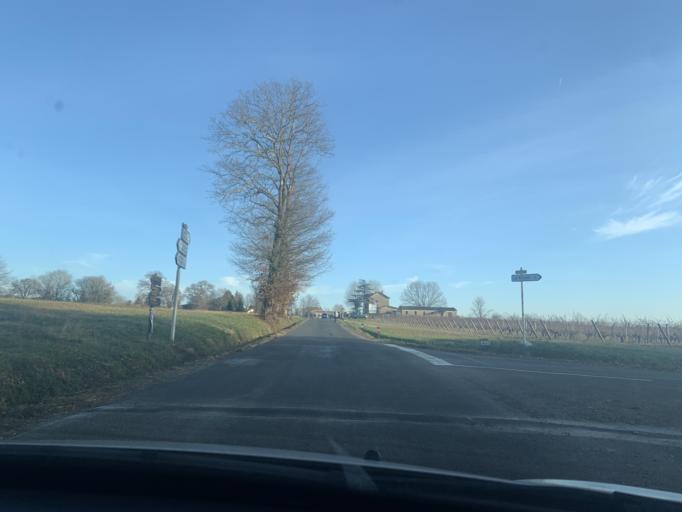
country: FR
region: Aquitaine
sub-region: Departement de la Gironde
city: Langon
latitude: 44.4943
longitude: -0.2661
